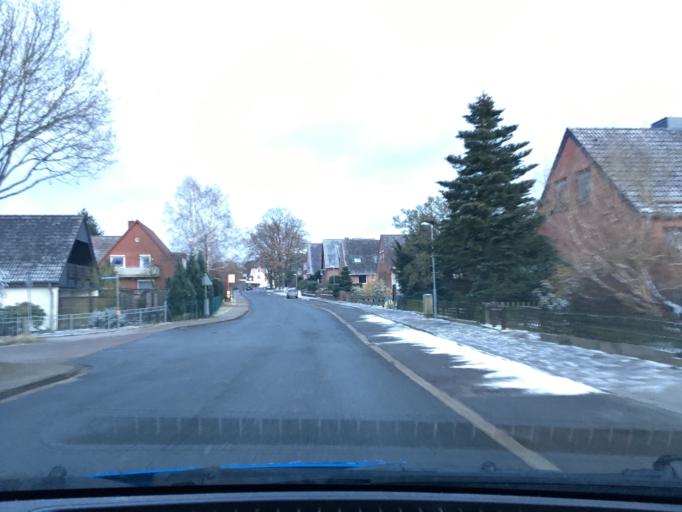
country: DE
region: Lower Saxony
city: Lueneburg
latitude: 53.2232
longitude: 10.3831
